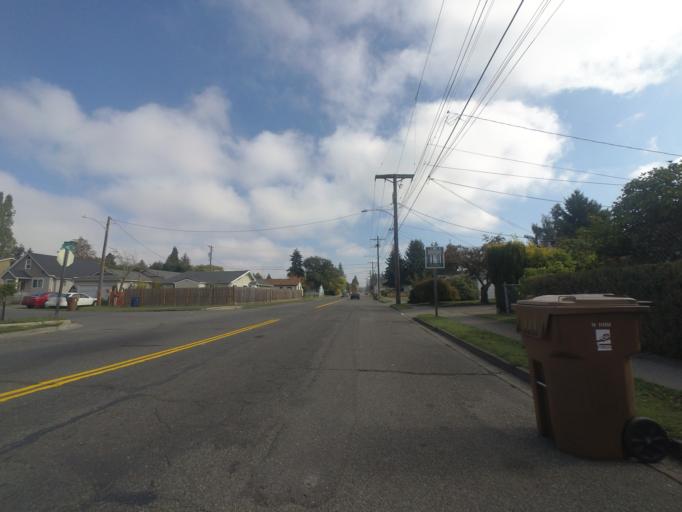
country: US
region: Washington
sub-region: Pierce County
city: Lakewood
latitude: 47.1974
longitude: -122.5050
